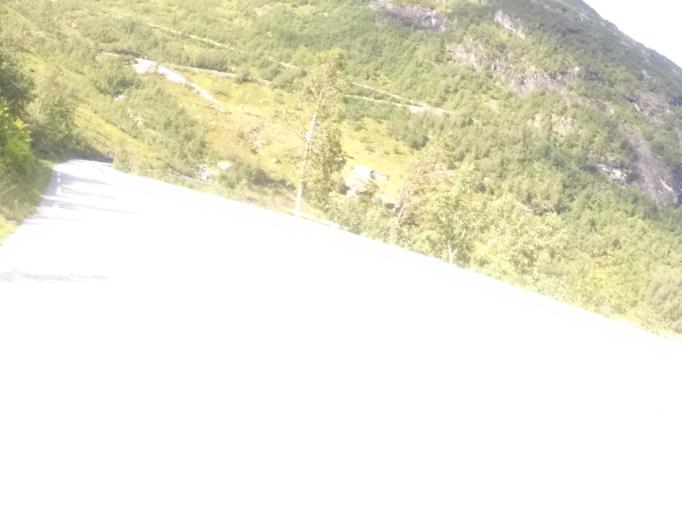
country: NO
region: Sogn og Fjordane
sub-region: Balestrand
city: Balestrand
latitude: 61.3531
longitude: 6.5232
